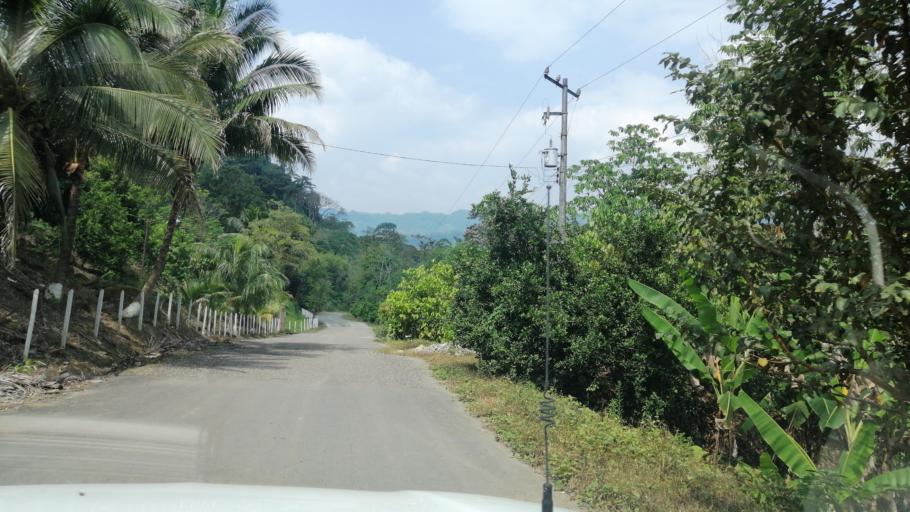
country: MX
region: Chiapas
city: Ostuacan
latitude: 17.3905
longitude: -93.3303
